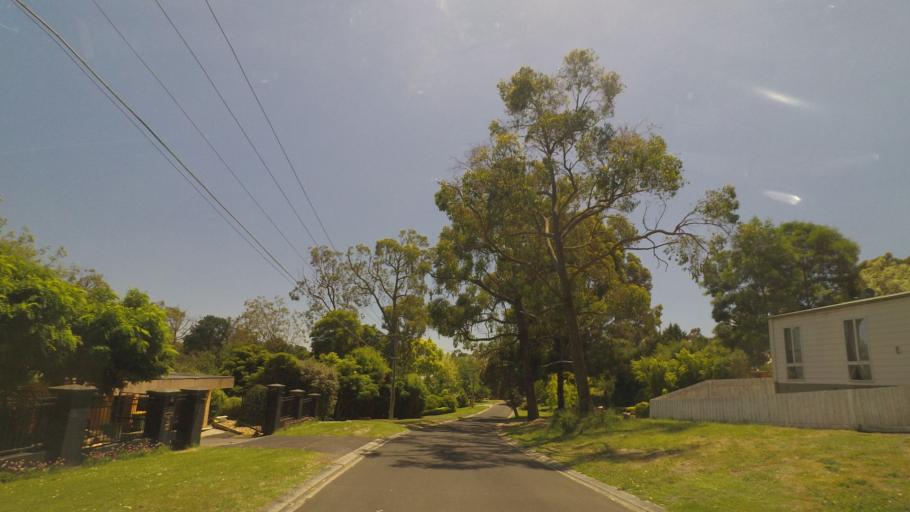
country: AU
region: Victoria
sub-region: Yarra Ranges
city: Montrose
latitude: -37.8087
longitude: 145.3574
